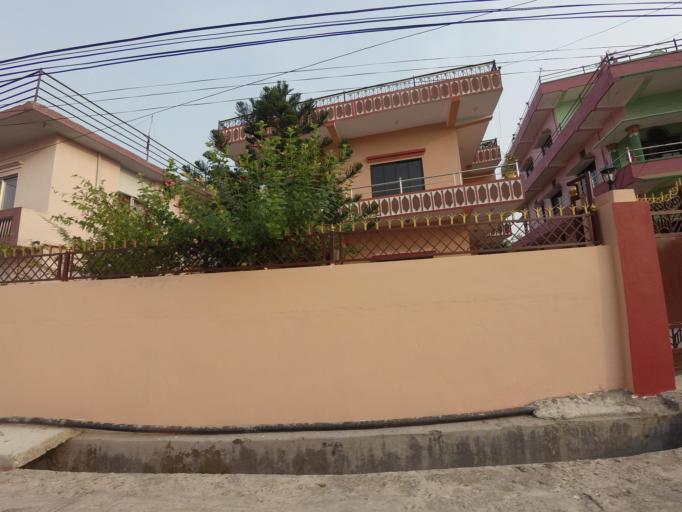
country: NP
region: Western Region
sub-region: Lumbini Zone
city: Bhairahawa
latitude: 27.5128
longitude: 83.4584
